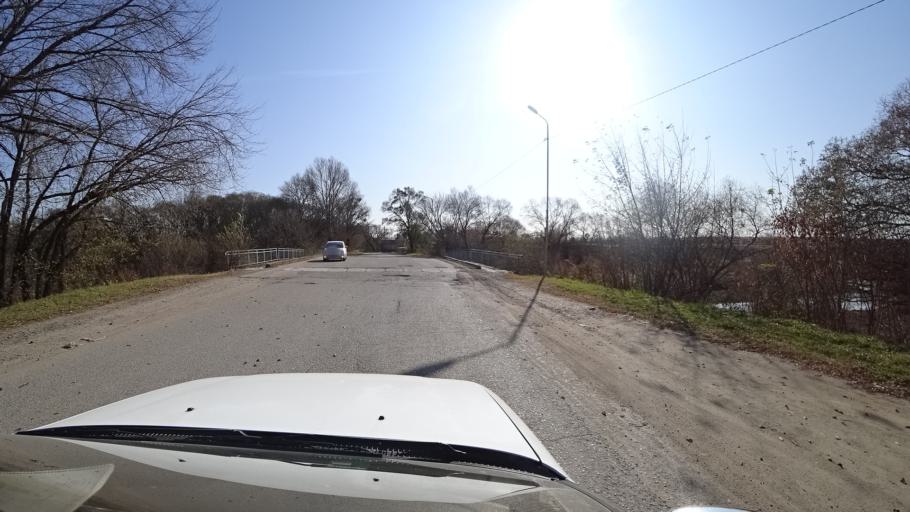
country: RU
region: Primorskiy
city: Dal'nerechensk
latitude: 45.9300
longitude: 133.7227
